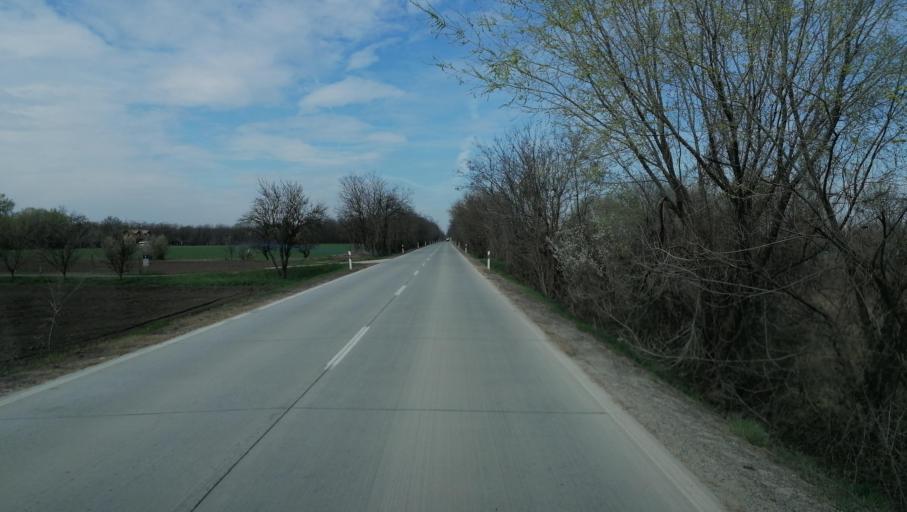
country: HU
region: Pest
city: Dunavarsany
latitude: 47.2582
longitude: 19.0355
